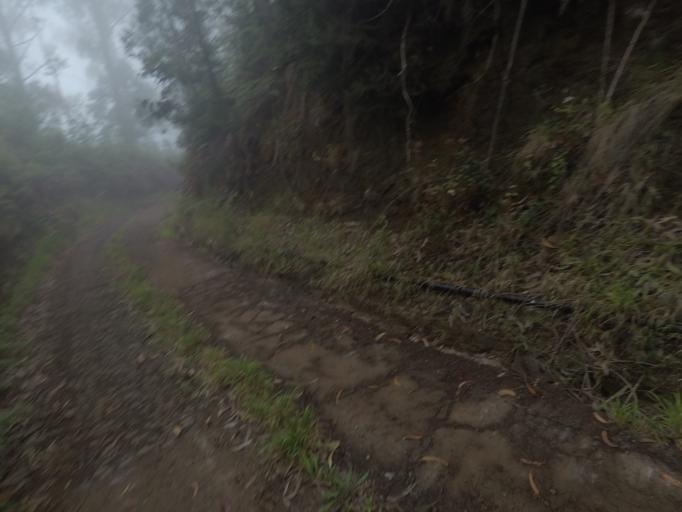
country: PT
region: Madeira
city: Ponta do Sol
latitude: 32.7142
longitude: -17.0935
